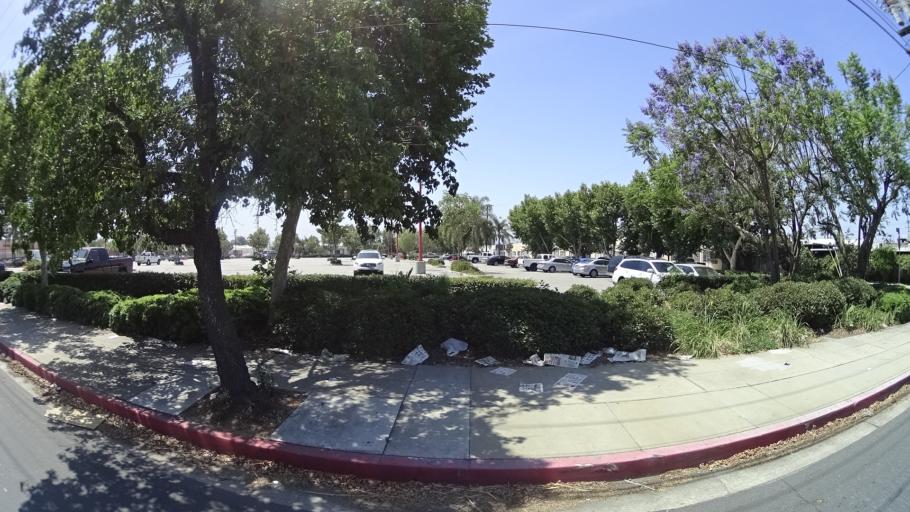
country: US
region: California
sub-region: Los Angeles County
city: Van Nuys
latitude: 34.2137
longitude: -118.4616
